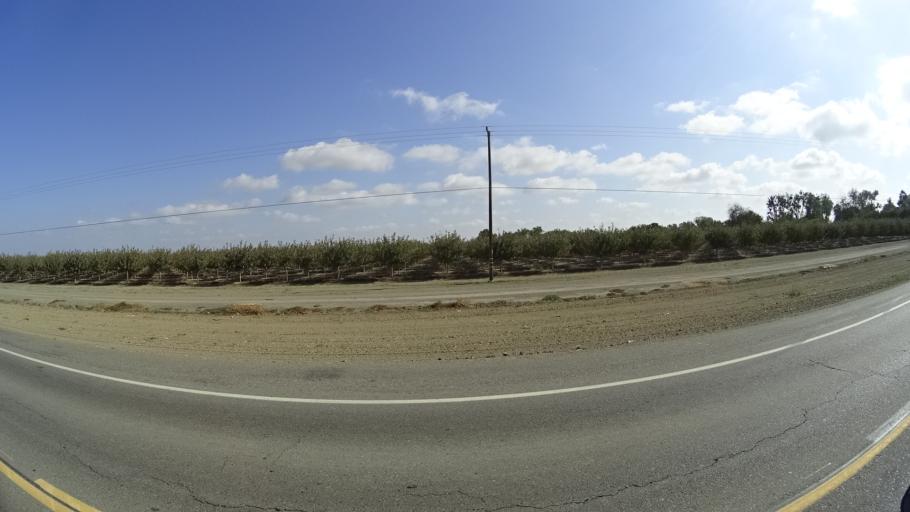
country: US
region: California
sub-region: Yolo County
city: Woodland
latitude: 38.7299
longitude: -121.7299
